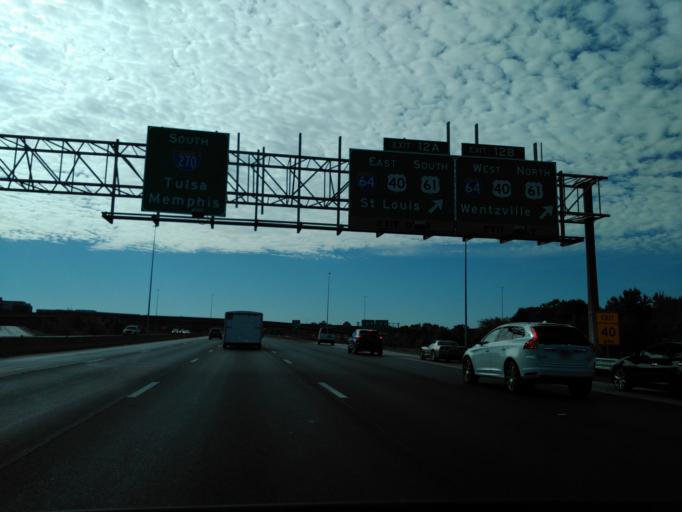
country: US
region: Missouri
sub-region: Saint Louis County
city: Creve Coeur
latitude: 38.6431
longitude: -90.4493
